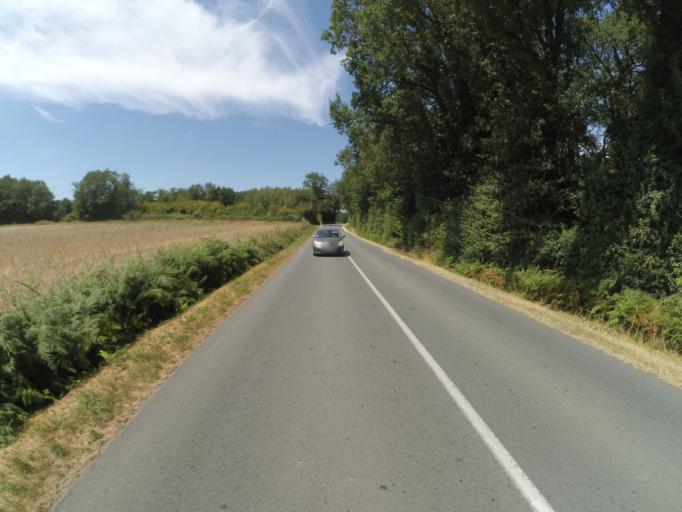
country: FR
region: Poitou-Charentes
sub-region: Departement de la Vienne
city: Saint-Maurice-la-Clouere
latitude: 46.3481
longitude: 0.4528
